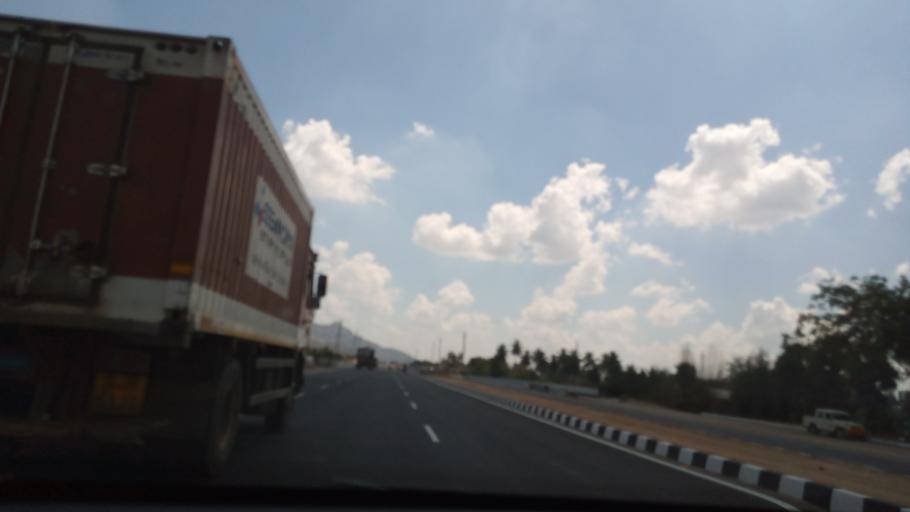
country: IN
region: Andhra Pradesh
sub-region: Chittoor
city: Pakala
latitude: 13.3658
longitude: 79.0892
